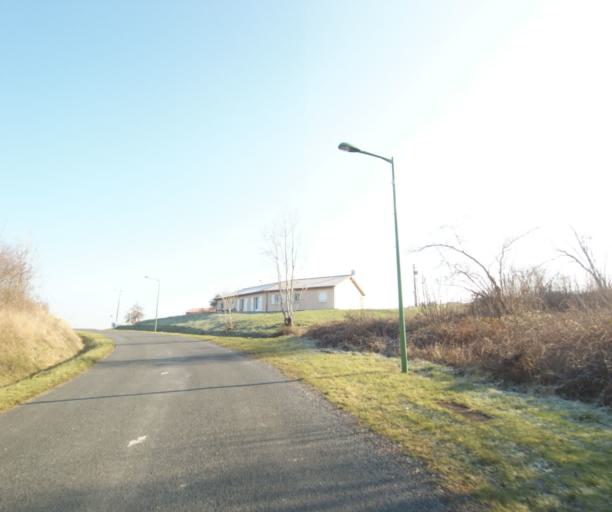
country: FR
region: Champagne-Ardenne
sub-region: Departement de la Haute-Marne
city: Chevillon
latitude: 48.4921
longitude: 5.0716
